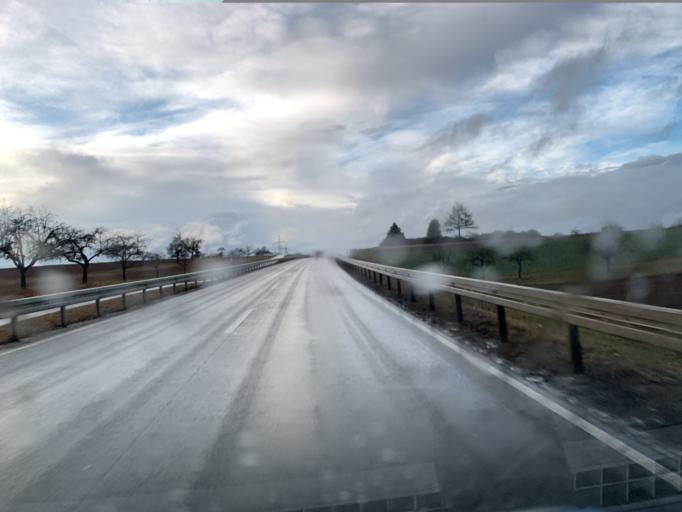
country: DE
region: Baden-Wuerttemberg
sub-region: Regierungsbezirk Stuttgart
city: Magstadt
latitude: 48.7348
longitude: 8.9593
